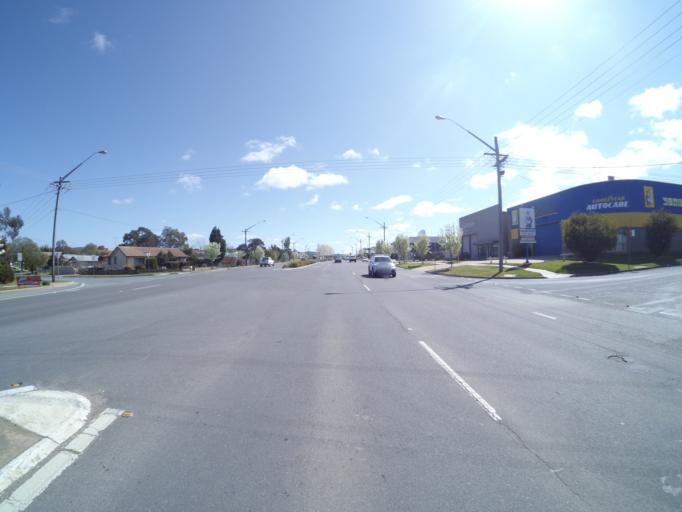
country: AU
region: New South Wales
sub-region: Queanbeyan
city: Queanbeyan
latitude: -35.3428
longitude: 149.2446
